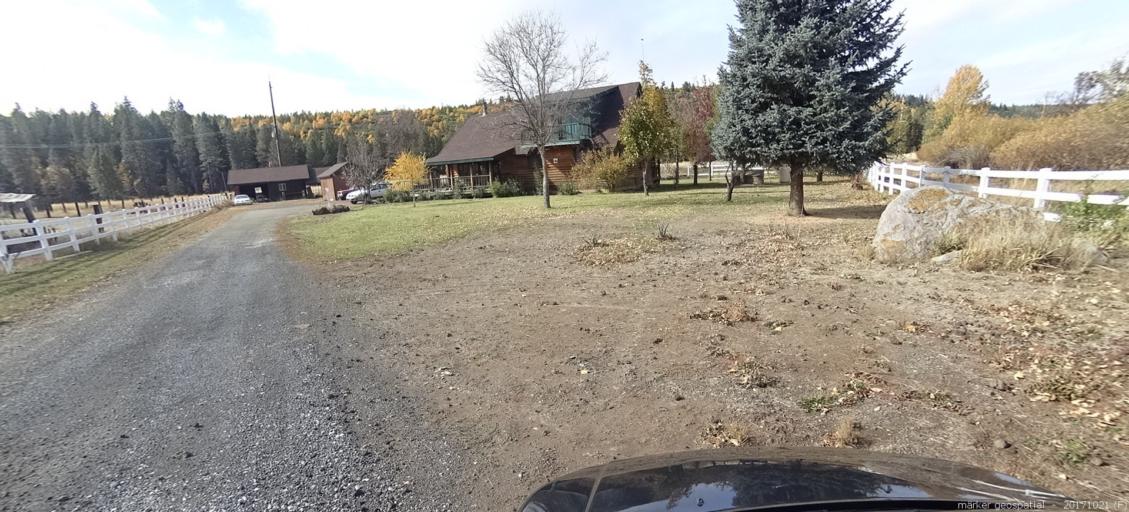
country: US
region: California
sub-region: Shasta County
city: Burney
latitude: 40.8899
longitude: -121.6701
